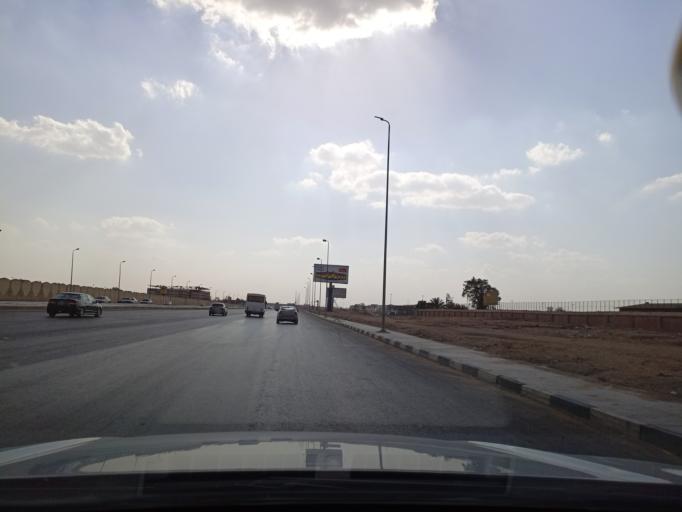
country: EG
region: Muhafazat al Qalyubiyah
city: Al Khankah
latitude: 30.1546
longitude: 31.4440
